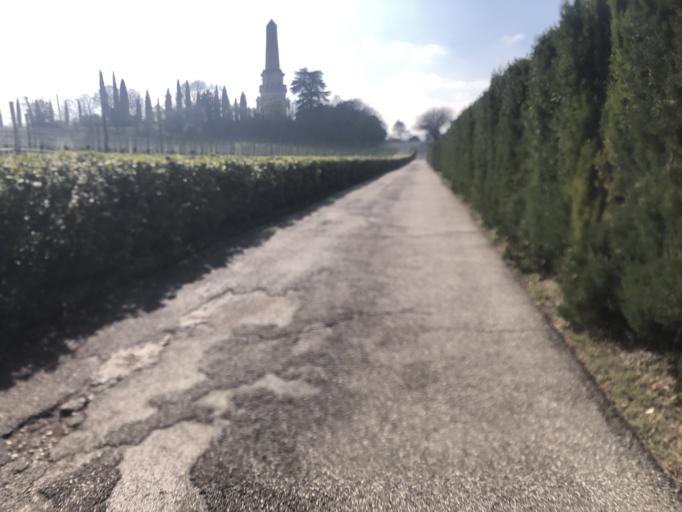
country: IT
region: Veneto
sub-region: Provincia di Verona
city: Rosegaferro
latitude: 45.3807
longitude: 10.7938
